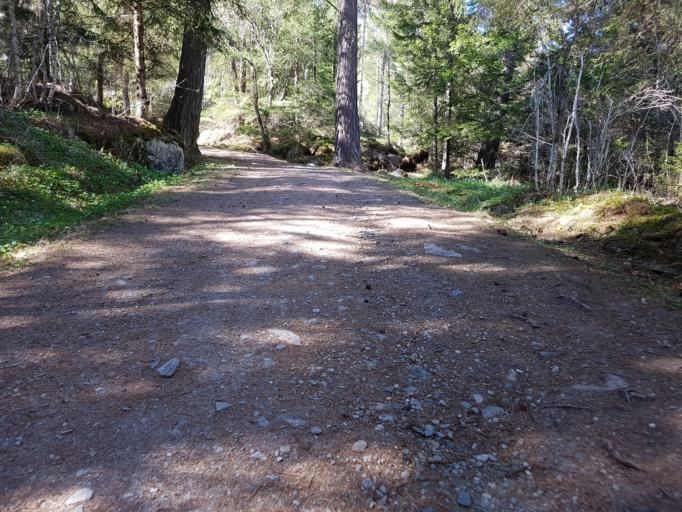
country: NO
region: Sor-Trondelag
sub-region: Trondheim
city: Trondheim
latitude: 63.4383
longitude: 10.3414
